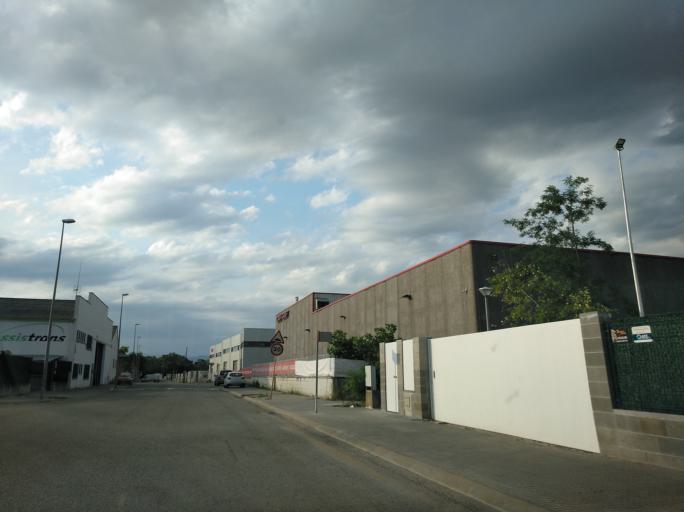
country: ES
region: Catalonia
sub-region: Provincia de Girona
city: Vilablareix
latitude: 41.9677
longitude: 2.7767
